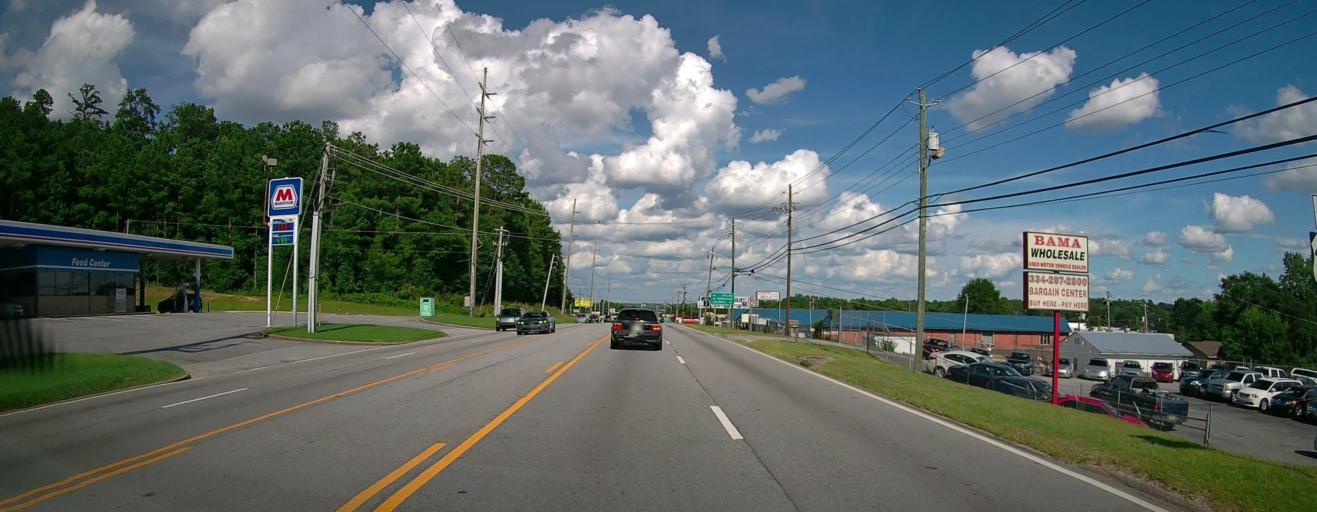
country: US
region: Alabama
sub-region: Russell County
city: Phenix City
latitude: 32.4753
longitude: -85.0347
